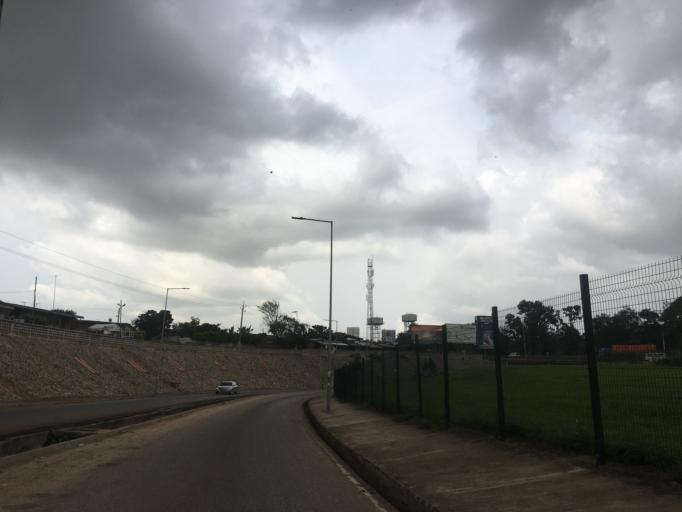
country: GH
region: Ashanti
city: Mamponteng
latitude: 6.6875
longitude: -1.5724
